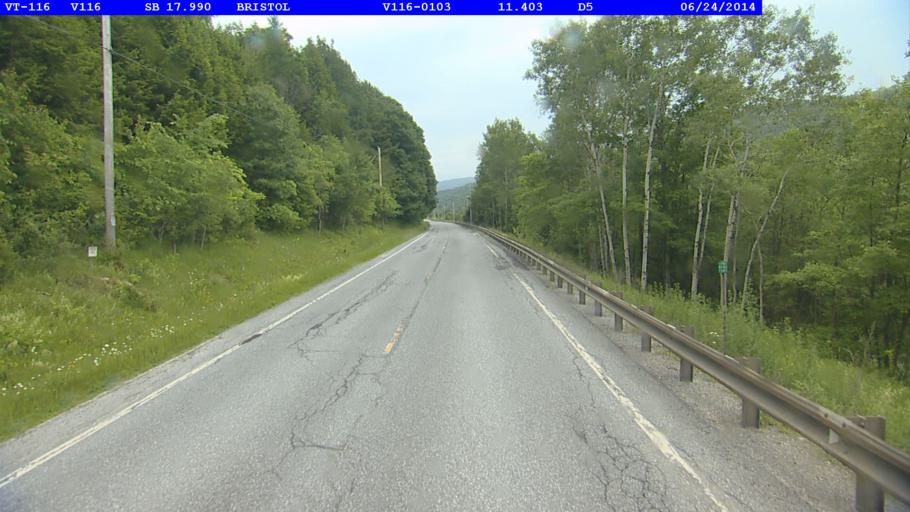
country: US
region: Vermont
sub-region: Addison County
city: Bristol
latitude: 44.1732
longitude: -73.0568
